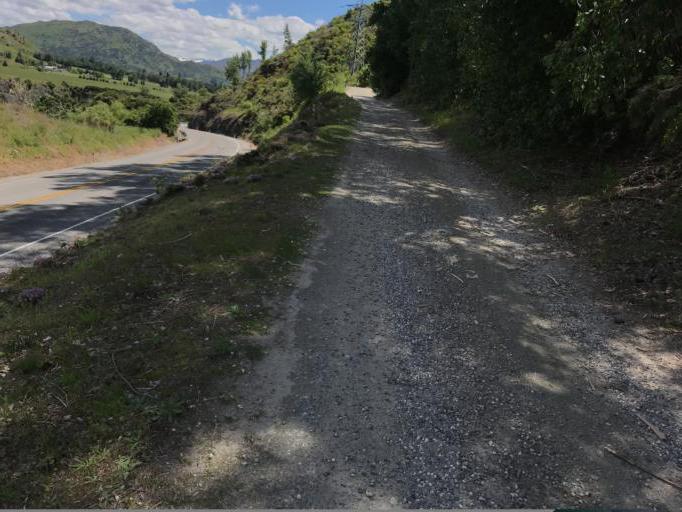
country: NZ
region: Otago
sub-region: Queenstown-Lakes District
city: Arrowtown
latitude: -45.0073
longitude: 168.8842
